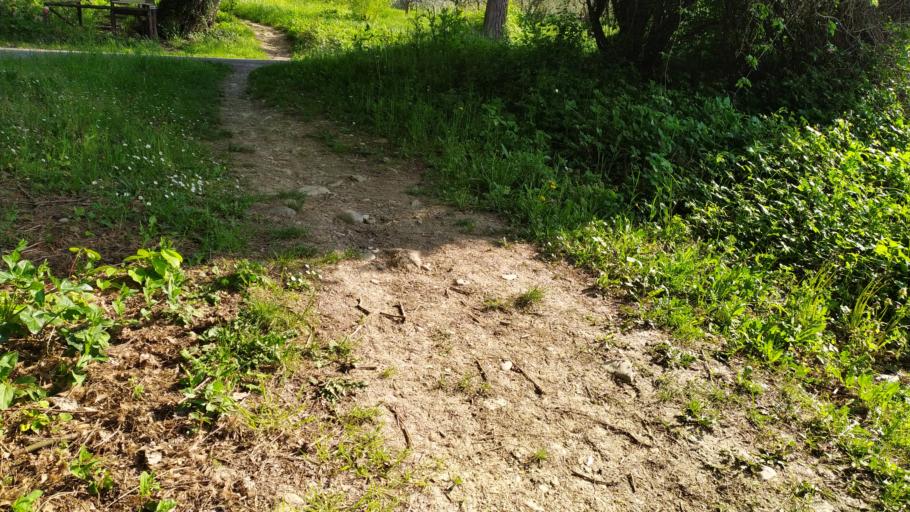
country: IT
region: Emilia-Romagna
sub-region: Provincia di Bologna
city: Borgo Tossignano
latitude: 44.2750
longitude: 11.6003
